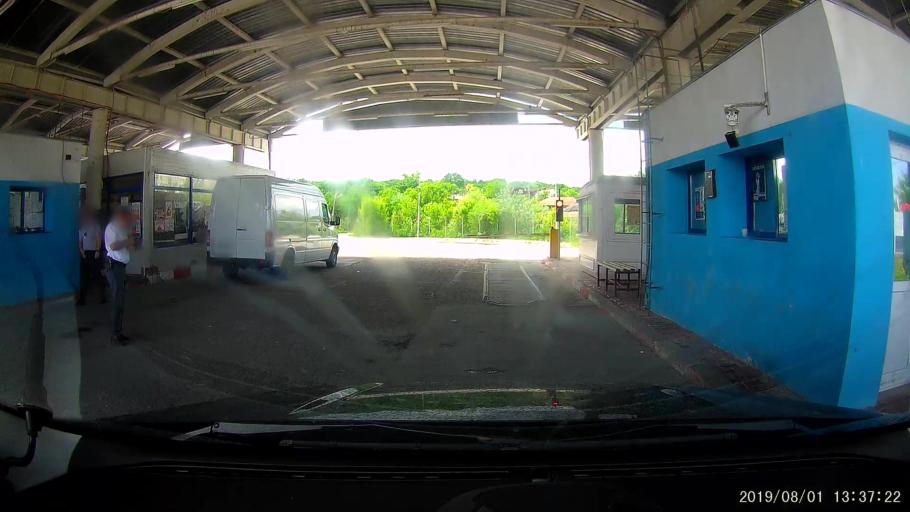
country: RO
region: Galati
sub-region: Comuna Oancea
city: Oancea
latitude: 45.9179
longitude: 28.1181
